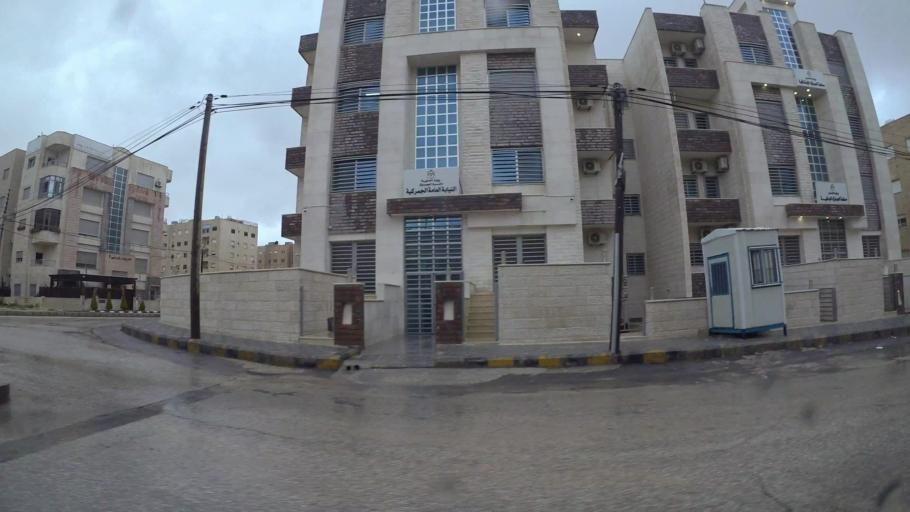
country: JO
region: Amman
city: Al Jubayhah
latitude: 32.0348
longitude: 35.8719
